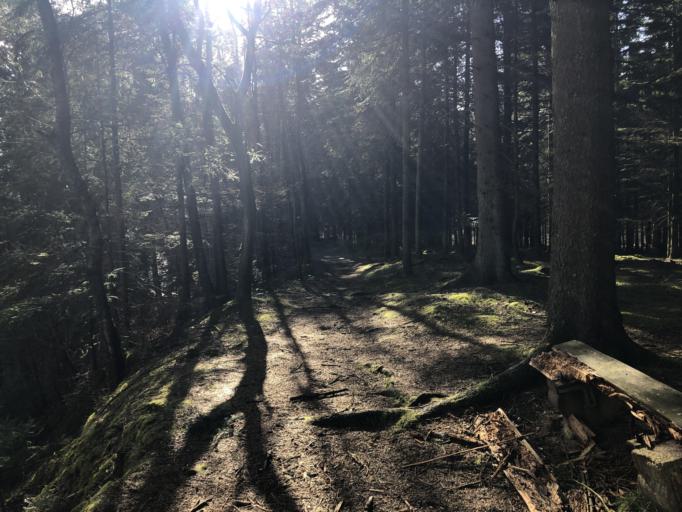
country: DK
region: Central Jutland
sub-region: Herning Kommune
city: Kibaek
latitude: 55.9506
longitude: 8.8764
